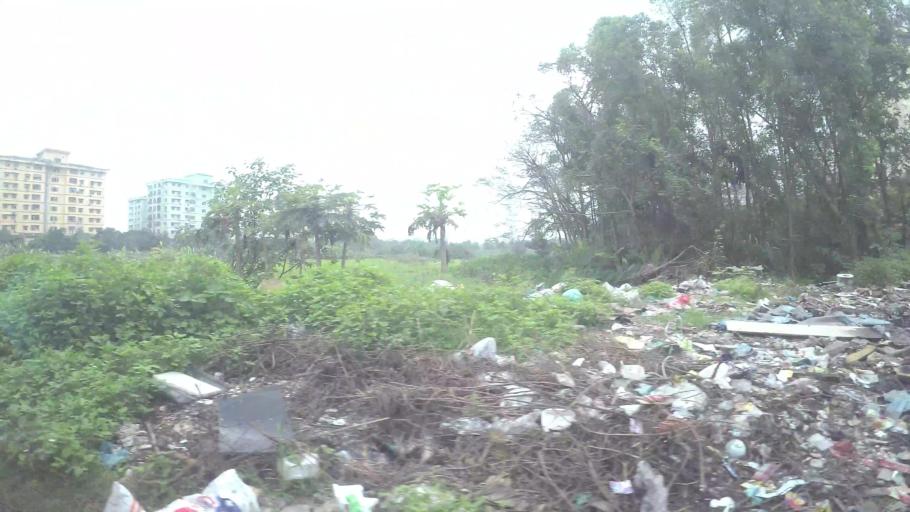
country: VN
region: Ha Noi
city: Van Dien
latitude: 20.9691
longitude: 105.8463
